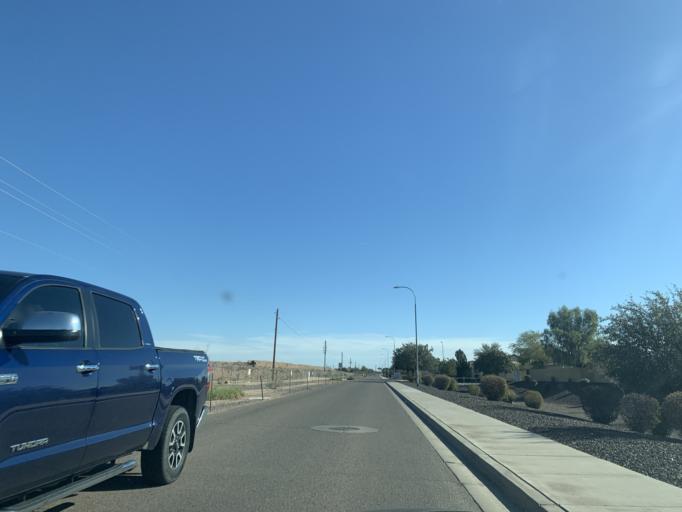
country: US
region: Arizona
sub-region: Maricopa County
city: Laveen
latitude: 33.3994
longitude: -112.1232
